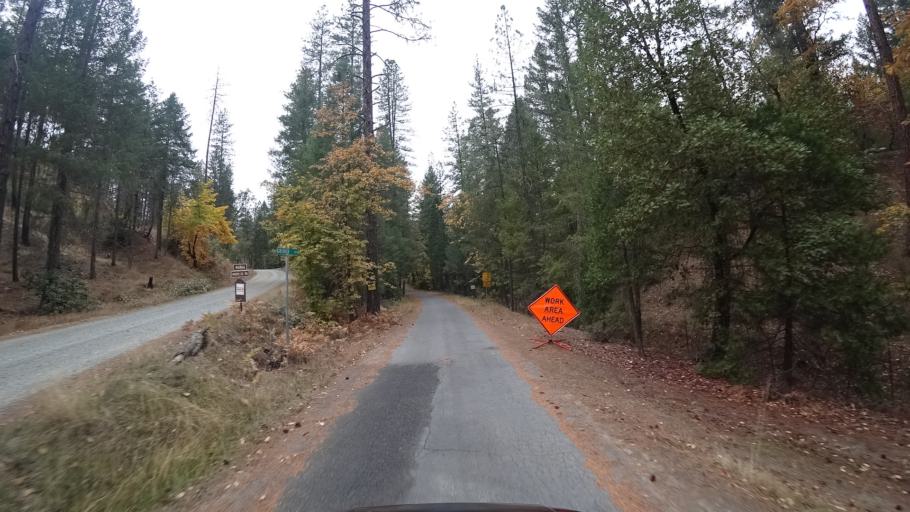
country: US
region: California
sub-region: Siskiyou County
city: Happy Camp
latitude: 41.8379
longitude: -123.2031
